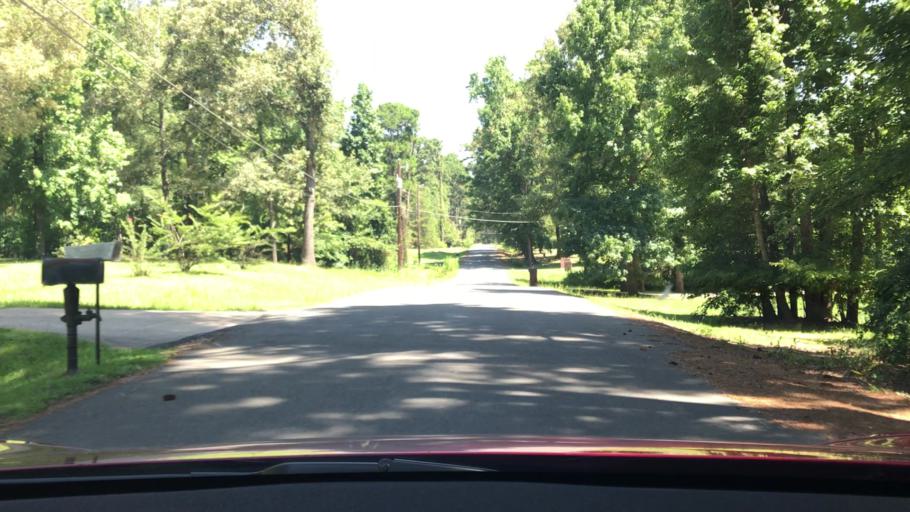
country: US
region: Louisiana
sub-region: De Soto Parish
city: Stonewall
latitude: 32.3428
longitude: -93.7085
